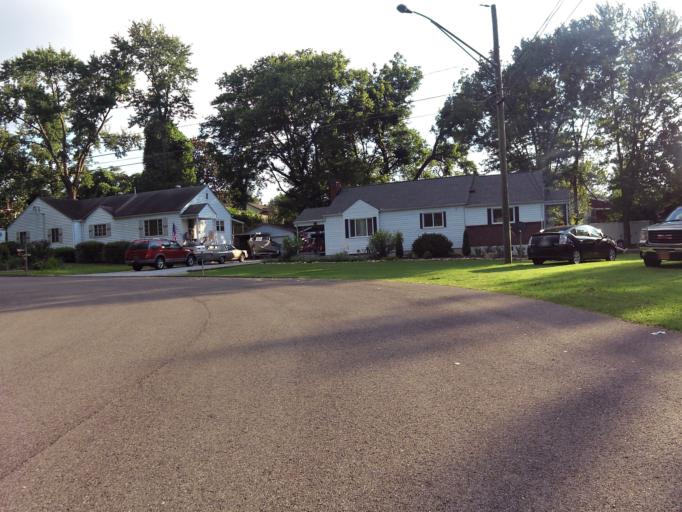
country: US
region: Tennessee
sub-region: Knox County
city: Knoxville
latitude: 36.0094
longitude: -83.9179
